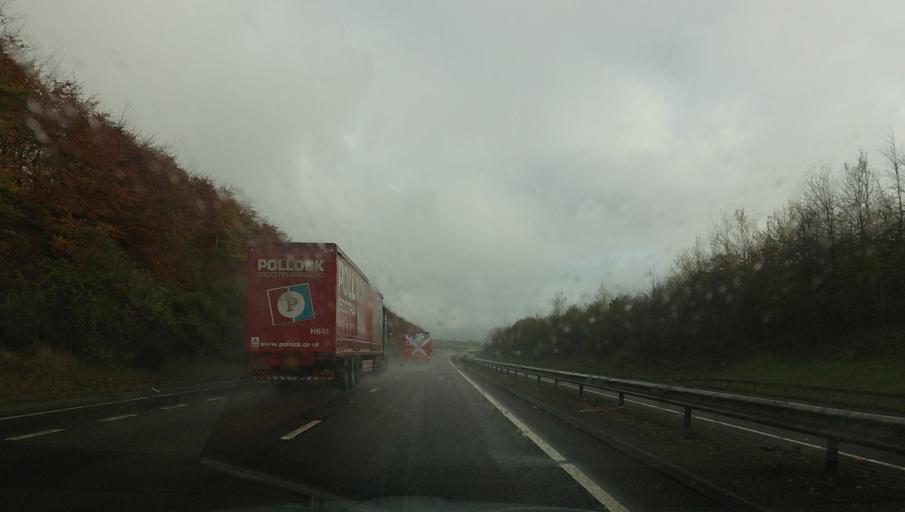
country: GB
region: Scotland
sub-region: Fife
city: Cowdenbeath
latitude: 56.1078
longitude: -3.3310
